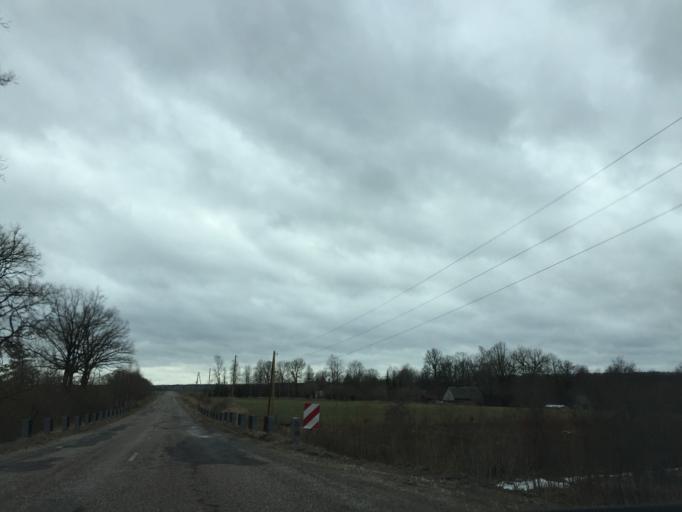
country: LV
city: Tervete
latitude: 56.5108
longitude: 23.4731
